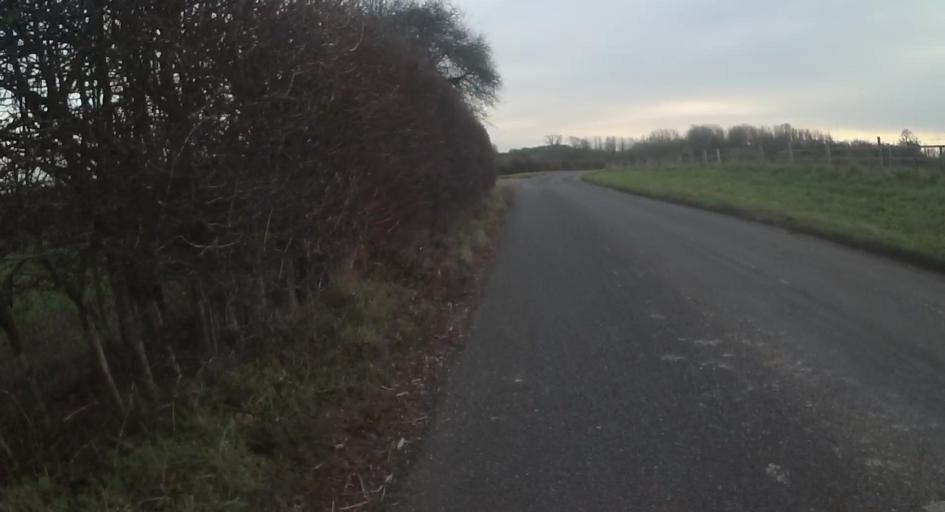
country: GB
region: England
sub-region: Hampshire
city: Overton
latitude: 51.2068
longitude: -1.3699
